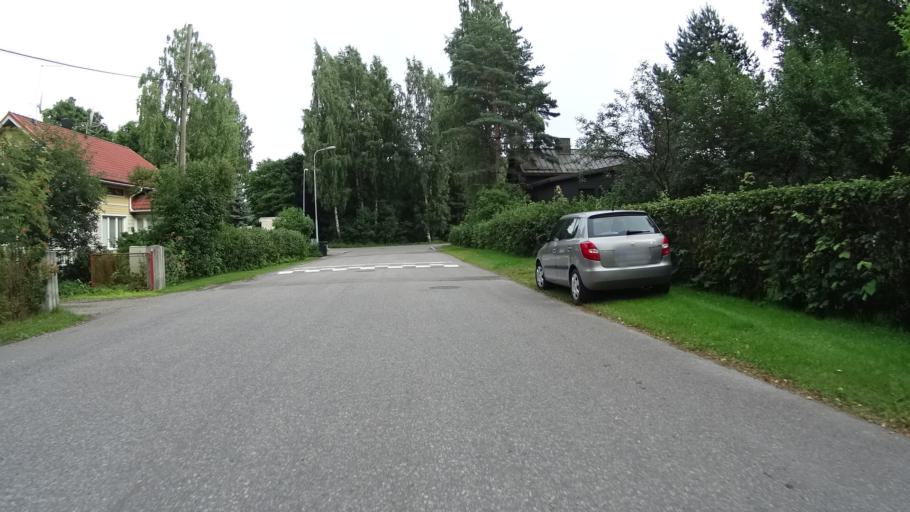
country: FI
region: Uusimaa
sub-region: Helsinki
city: Teekkarikylae
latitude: 60.2273
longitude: 24.8625
